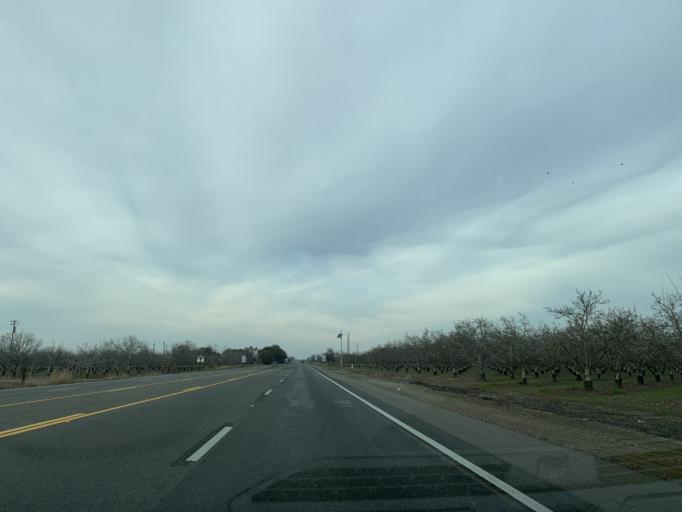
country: US
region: California
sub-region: Yuba County
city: Plumas Lake
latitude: 38.8872
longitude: -121.5719
